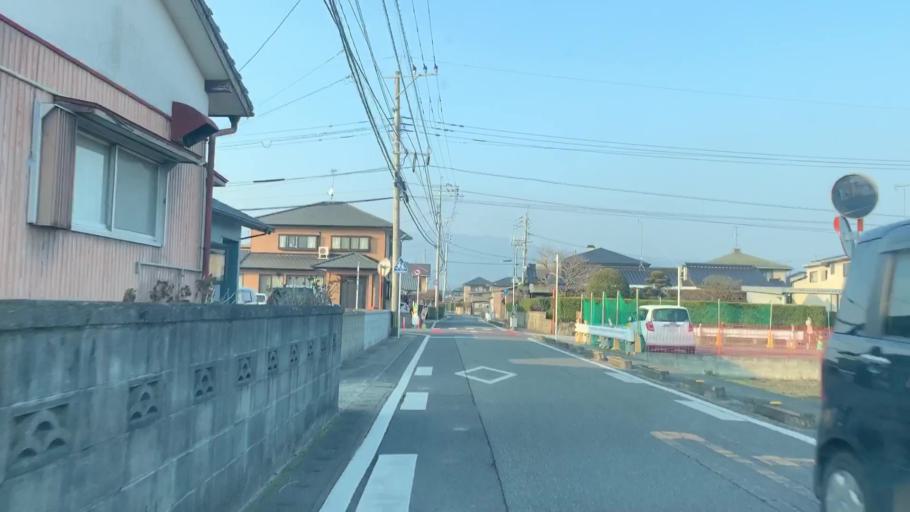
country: JP
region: Saga Prefecture
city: Saga-shi
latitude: 33.2702
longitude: 130.2295
